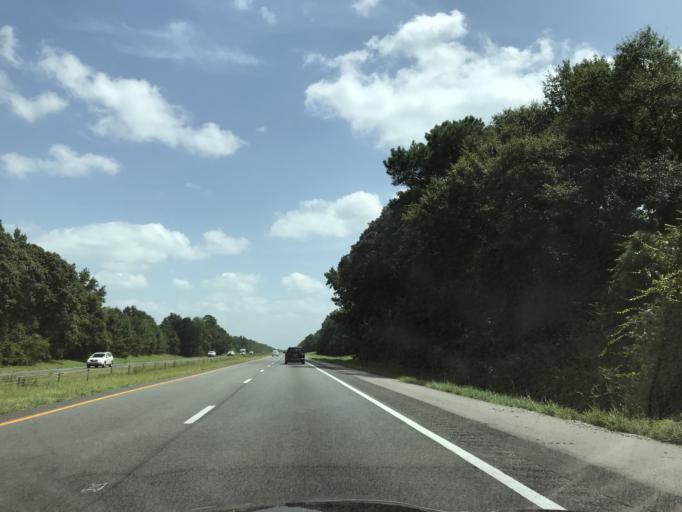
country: US
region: North Carolina
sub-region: Sampson County
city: Clinton
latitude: 35.2105
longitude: -78.3219
